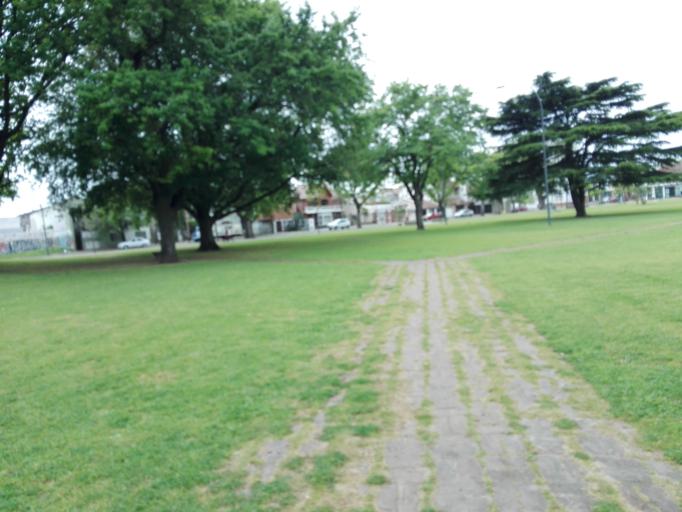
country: AR
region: Buenos Aires
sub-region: Partido de La Plata
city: La Plata
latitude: -34.9426
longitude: -57.9527
